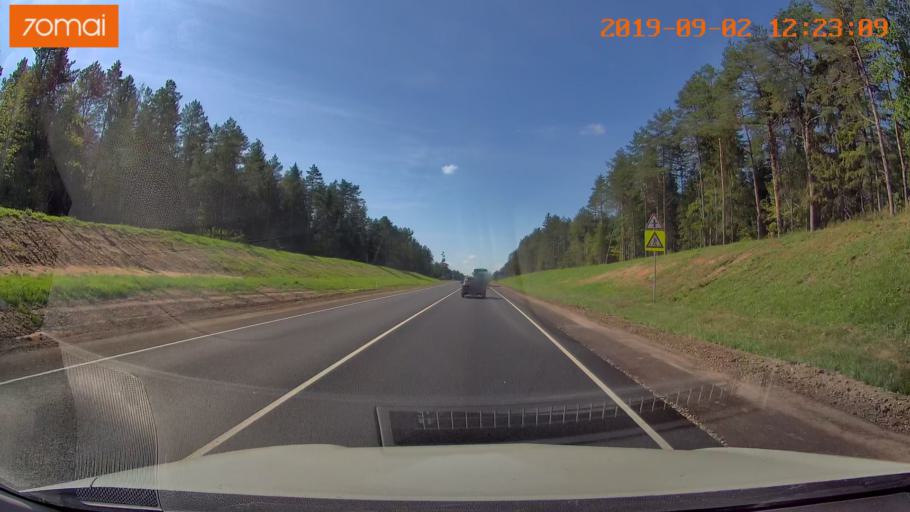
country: RU
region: Smolensk
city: Shumyachi
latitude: 53.8762
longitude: 32.6236
